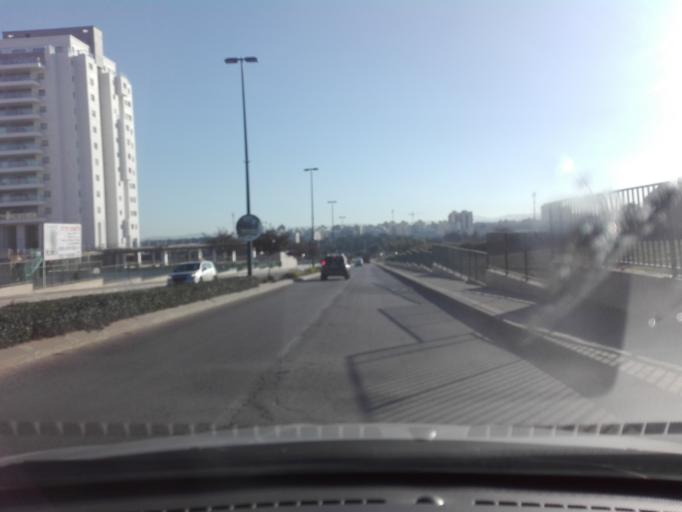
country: IL
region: Central District
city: Netanya
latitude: 32.3085
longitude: 34.8585
